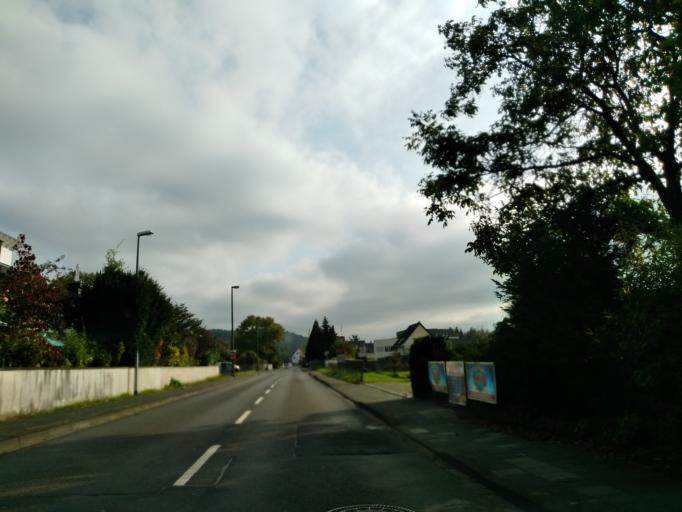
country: DE
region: North Rhine-Westphalia
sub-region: Regierungsbezirk Koln
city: Konigswinter
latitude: 50.7025
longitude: 7.1829
